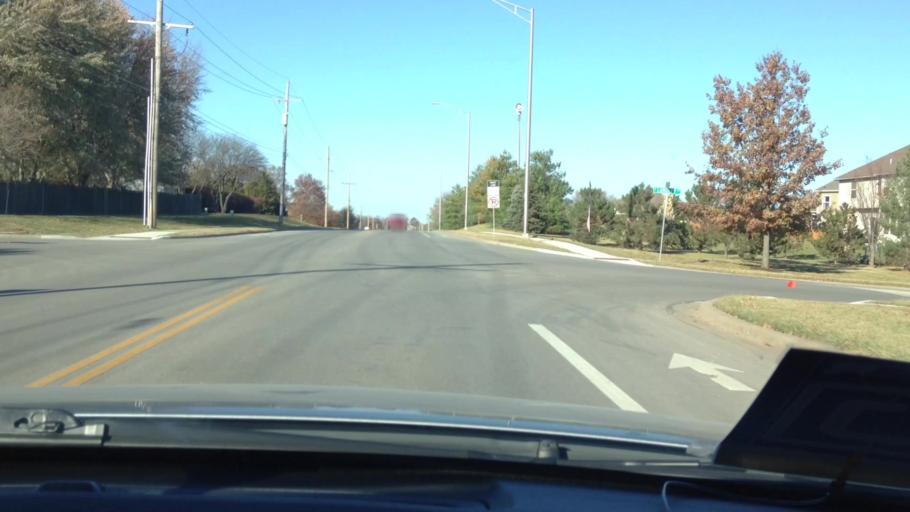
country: US
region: Kansas
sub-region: Johnson County
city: Olathe
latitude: 38.9077
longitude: -94.8160
